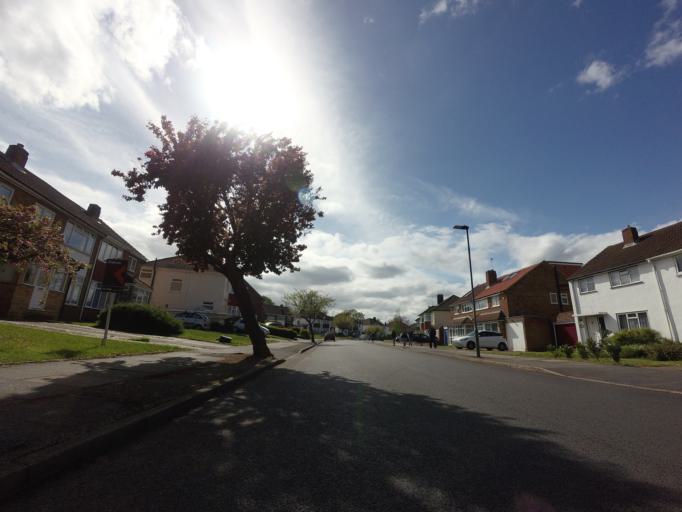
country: GB
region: England
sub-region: Greater London
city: Orpington
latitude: 51.3734
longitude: 0.1197
